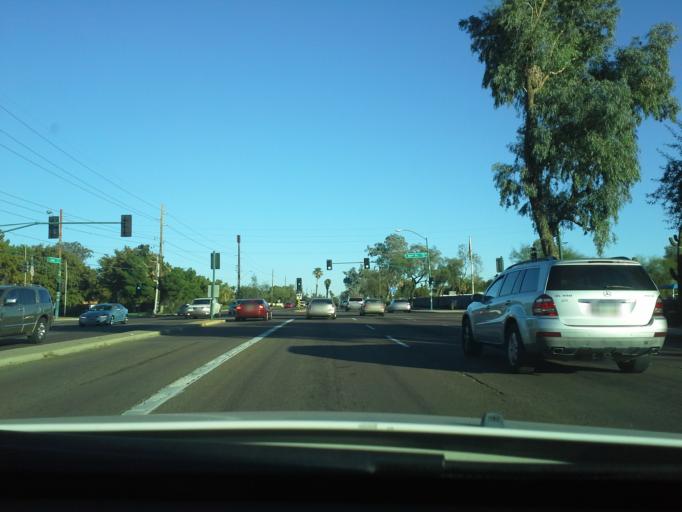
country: US
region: Arizona
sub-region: Maricopa County
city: Paradise Valley
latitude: 33.5826
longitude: -111.9613
